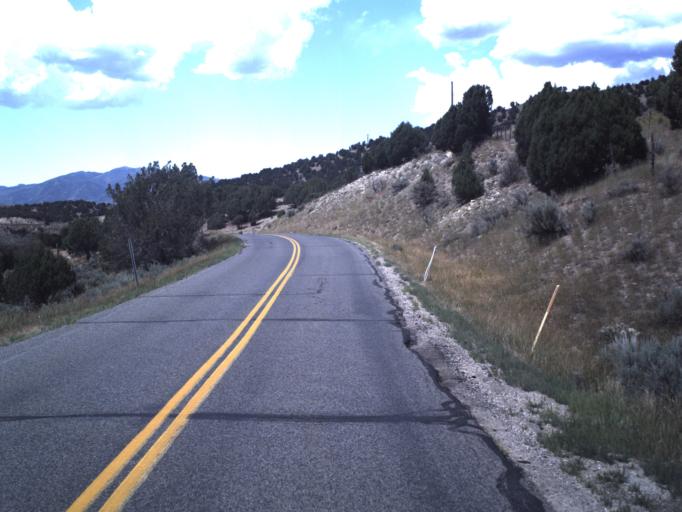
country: US
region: Utah
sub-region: Summit County
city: Oakley
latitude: 40.7589
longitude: -111.3747
